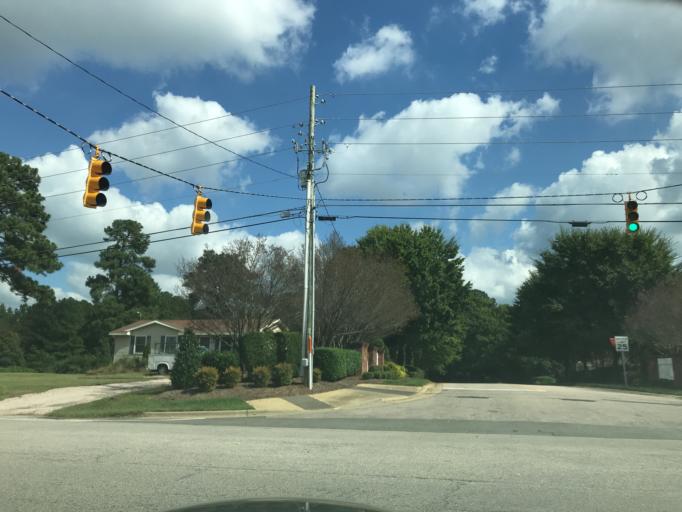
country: US
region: North Carolina
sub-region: Wake County
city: Knightdale
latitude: 35.8632
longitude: -78.5667
